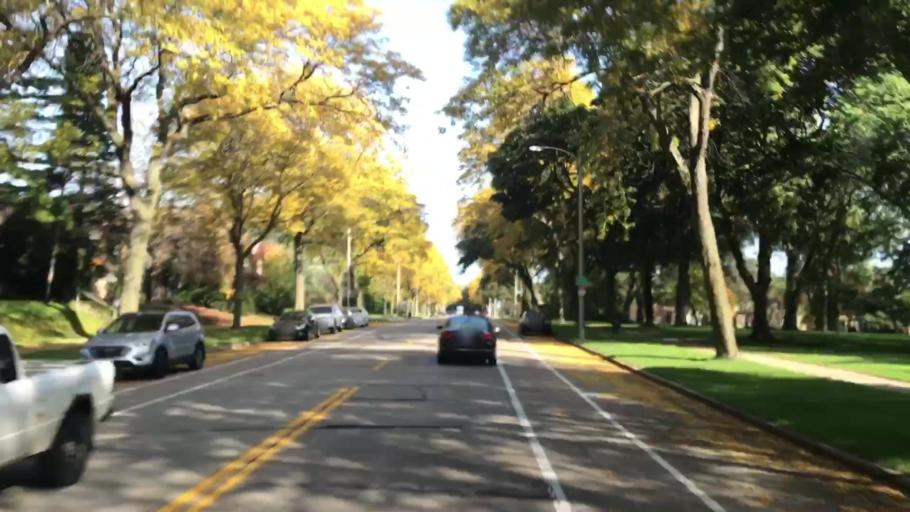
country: US
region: Wisconsin
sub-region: Milwaukee County
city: Shorewood
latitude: 43.0828
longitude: -87.8975
